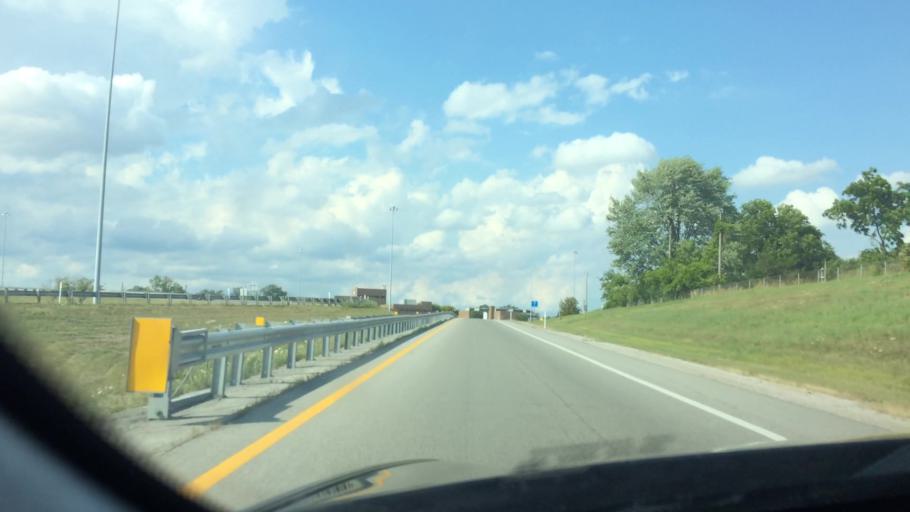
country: US
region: Ohio
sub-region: Lucas County
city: Maumee
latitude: 41.5521
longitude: -83.6838
